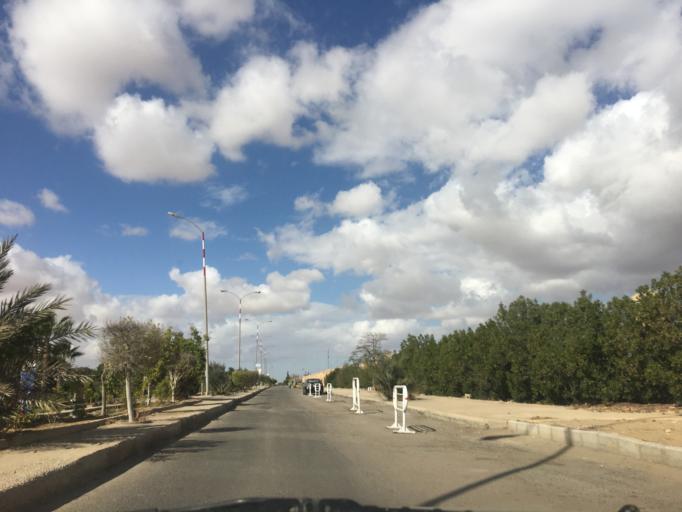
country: EG
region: Al Jizah
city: Madinat Sittah Uktubar
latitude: 29.9969
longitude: 30.9696
